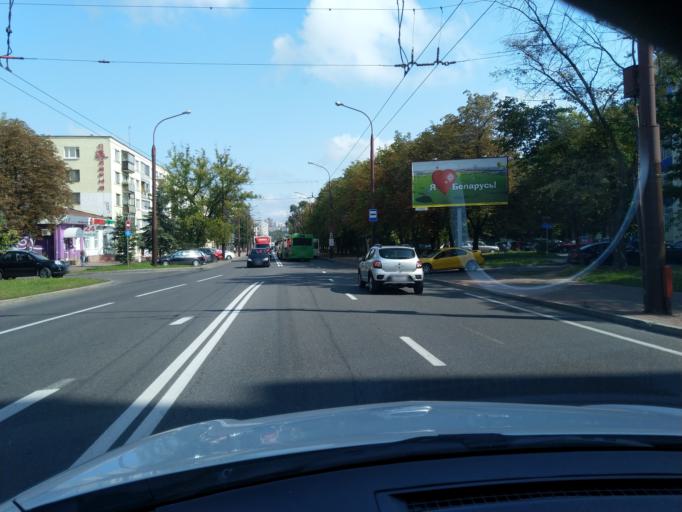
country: BY
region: Minsk
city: Minsk
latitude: 53.9168
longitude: 27.5725
